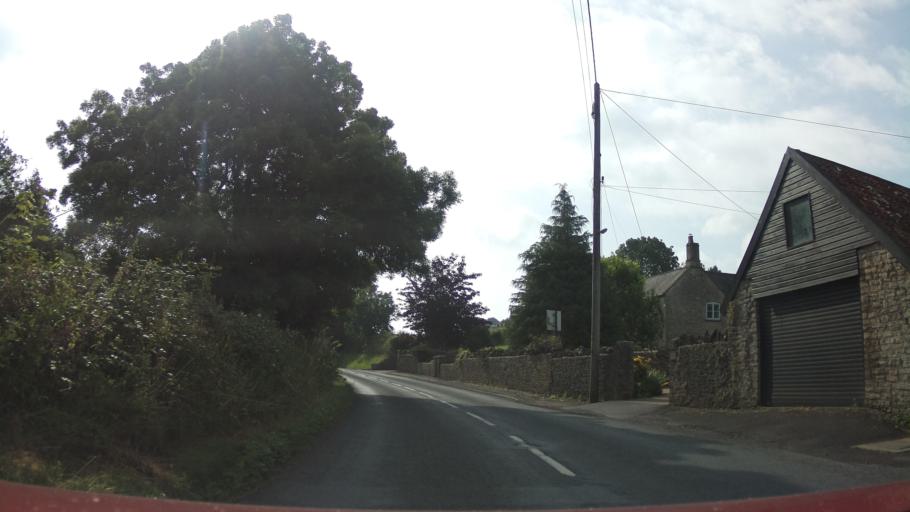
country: GB
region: England
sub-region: Bath and North East Somerset
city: East Harptree
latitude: 51.2802
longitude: -2.5862
